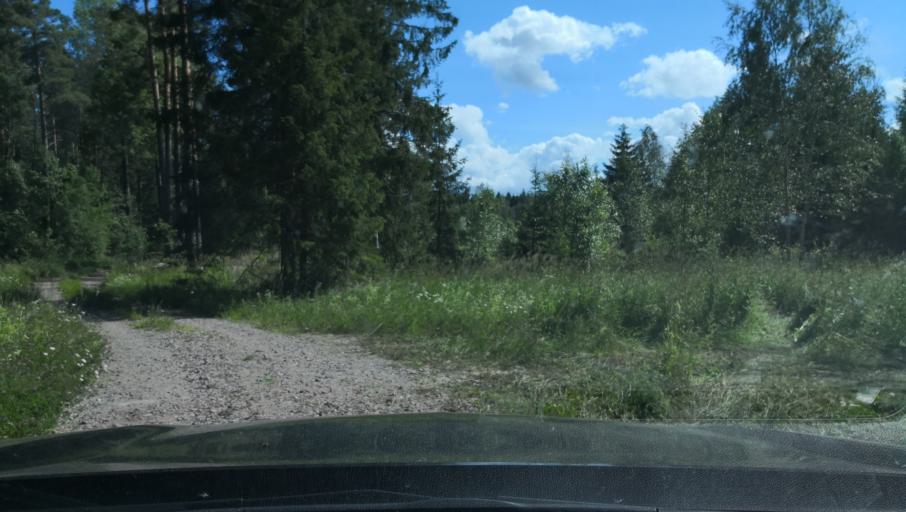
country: SE
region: Vaestmanland
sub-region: Kungsors Kommun
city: Kungsoer
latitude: 59.3429
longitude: 16.0593
